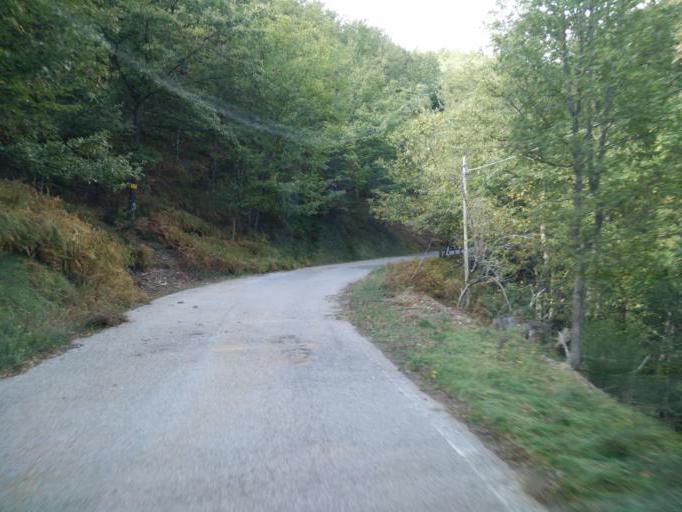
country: IT
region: Tuscany
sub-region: Provincia di Massa-Carrara
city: Patigno
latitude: 44.3452
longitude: 9.7051
